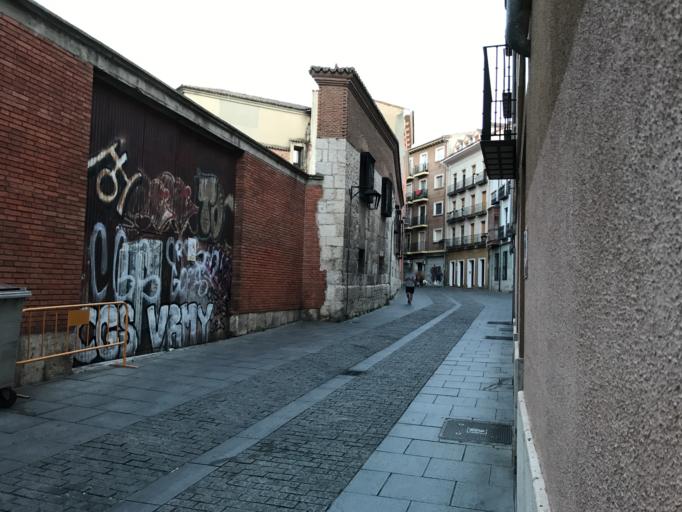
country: ES
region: Castille and Leon
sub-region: Provincia de Valladolid
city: Valladolid
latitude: 41.6565
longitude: -4.7293
